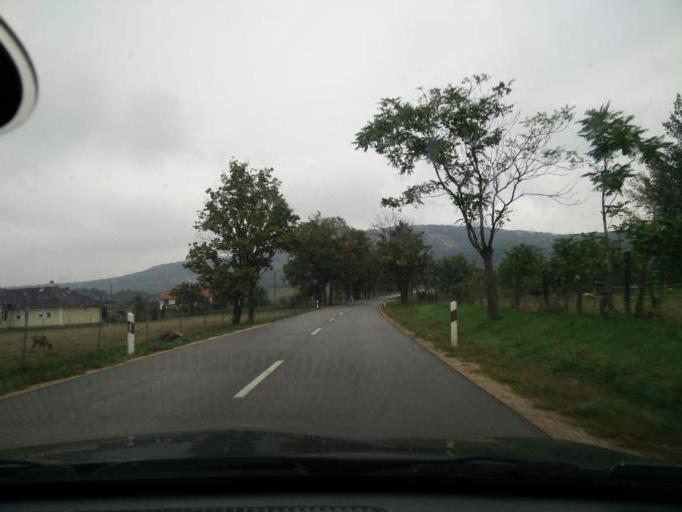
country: HU
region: Komarom-Esztergom
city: Tarjan
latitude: 47.6440
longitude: 18.5226
